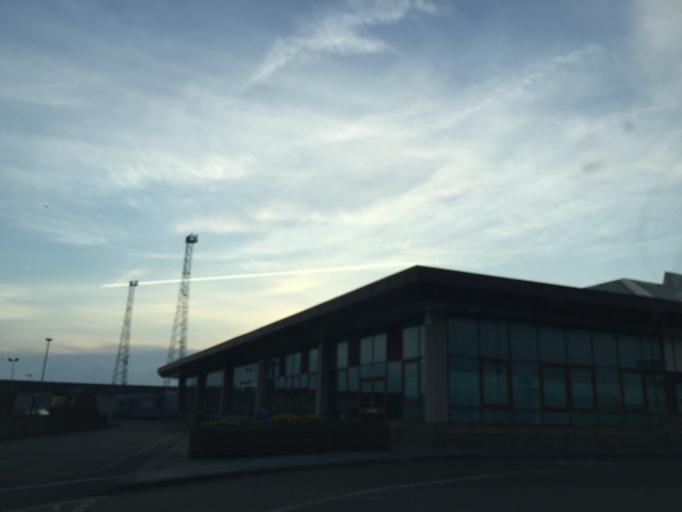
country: JE
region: St Helier
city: Saint Helier
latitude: 49.1792
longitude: -2.1160
